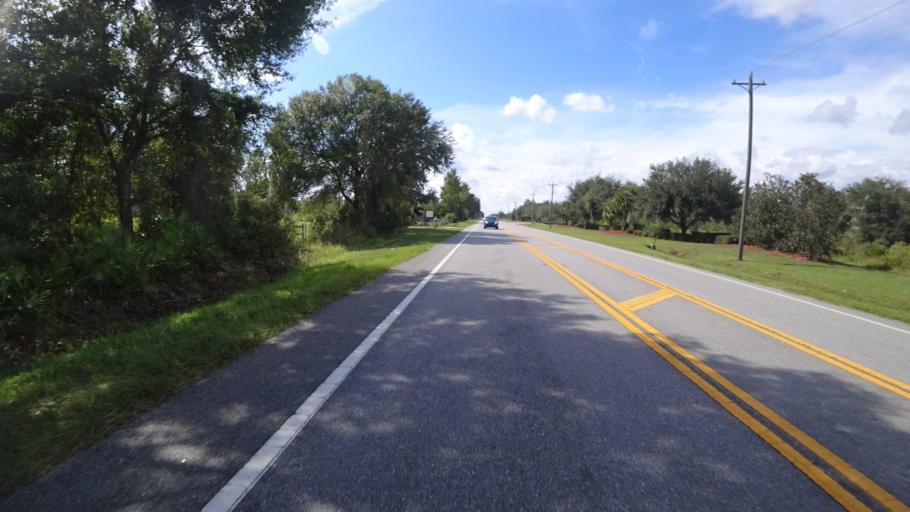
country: US
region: Florida
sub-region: Hillsborough County
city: Wimauma
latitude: 27.4599
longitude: -82.1191
